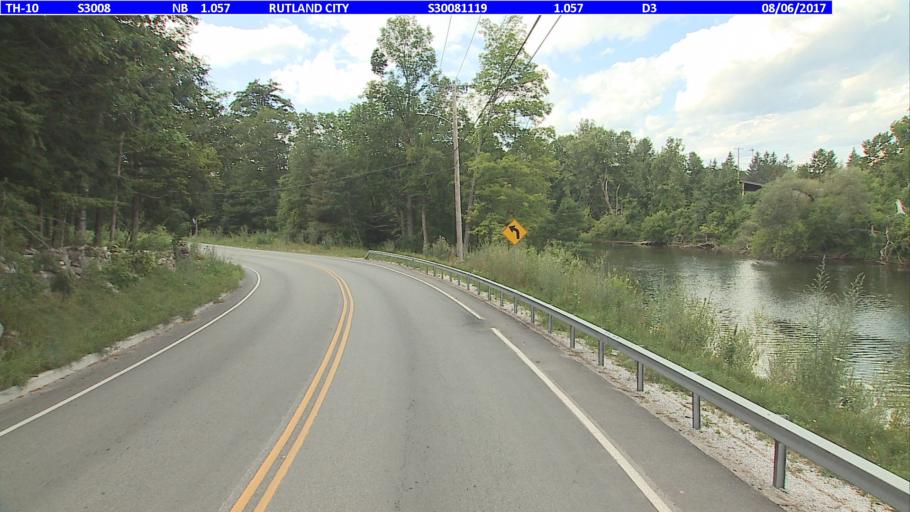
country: US
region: Vermont
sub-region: Rutland County
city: Rutland
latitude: 43.6014
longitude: -72.9932
